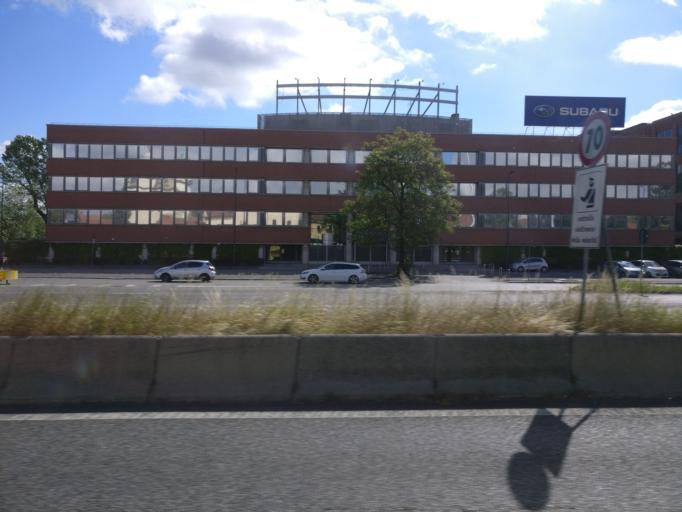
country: IT
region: Lombardy
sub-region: Citta metropolitana di Milano
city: Baranzate
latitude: 45.5021
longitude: 9.1302
